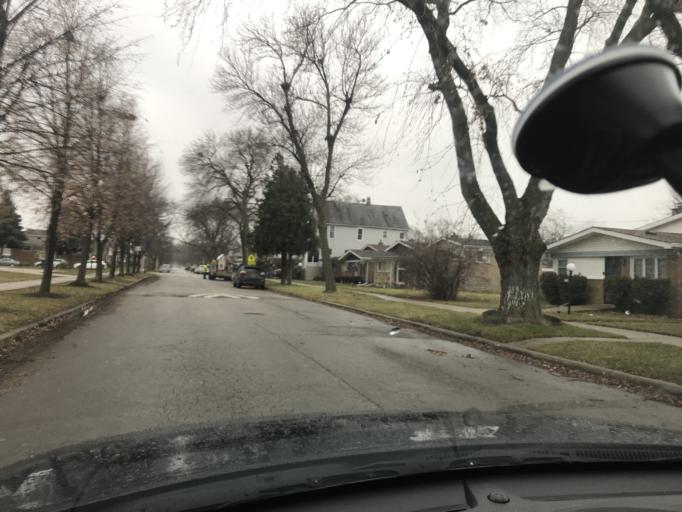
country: US
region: Illinois
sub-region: Cook County
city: Evergreen Park
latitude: 41.7243
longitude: -87.6396
